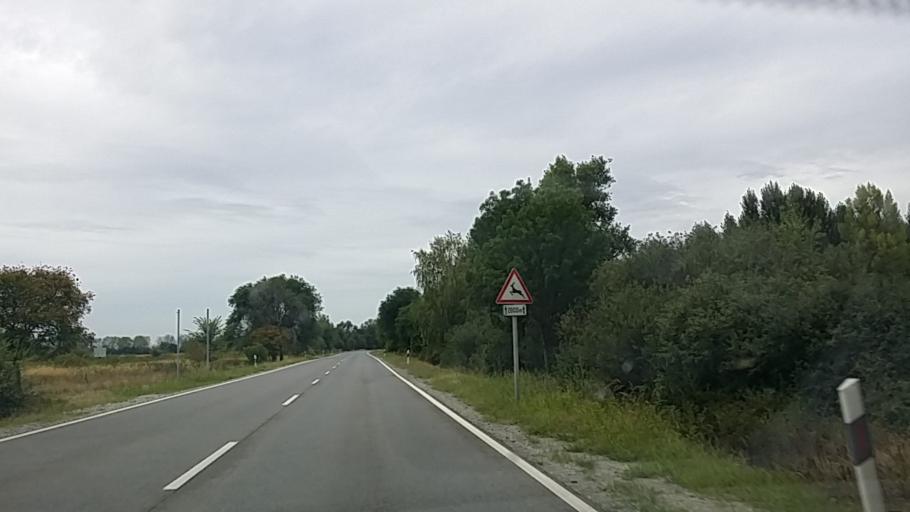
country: HU
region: Gyor-Moson-Sopron
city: Fertoszentmiklos
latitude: 47.5934
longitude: 16.8418
